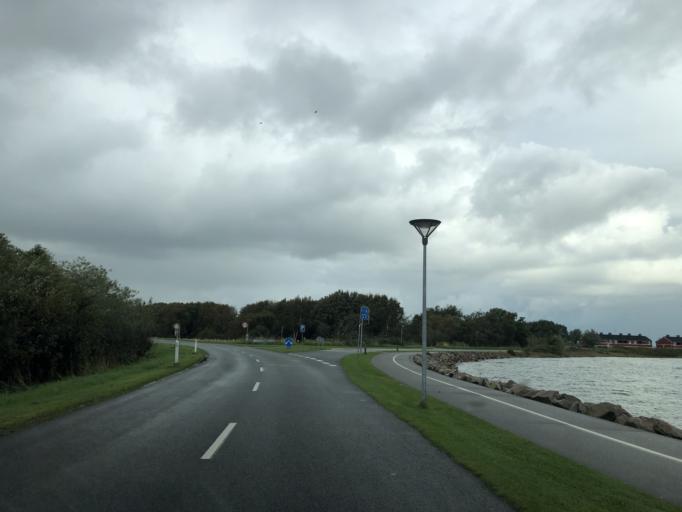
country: DK
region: Central Jutland
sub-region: Lemvig Kommune
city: Lemvig
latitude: 56.5613
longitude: 8.2943
